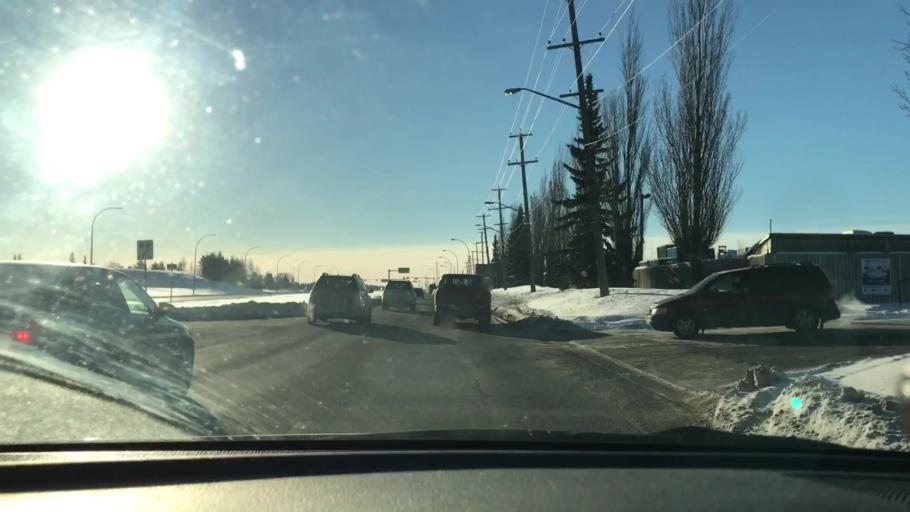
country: CA
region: Alberta
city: Edmonton
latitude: 53.4868
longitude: -113.4674
